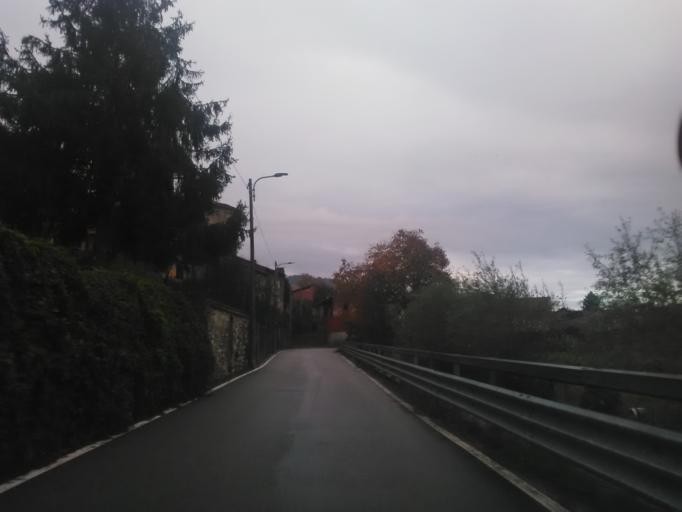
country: IT
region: Piedmont
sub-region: Provincia di Vercelli
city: Gattinara
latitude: 45.6137
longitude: 8.3749
